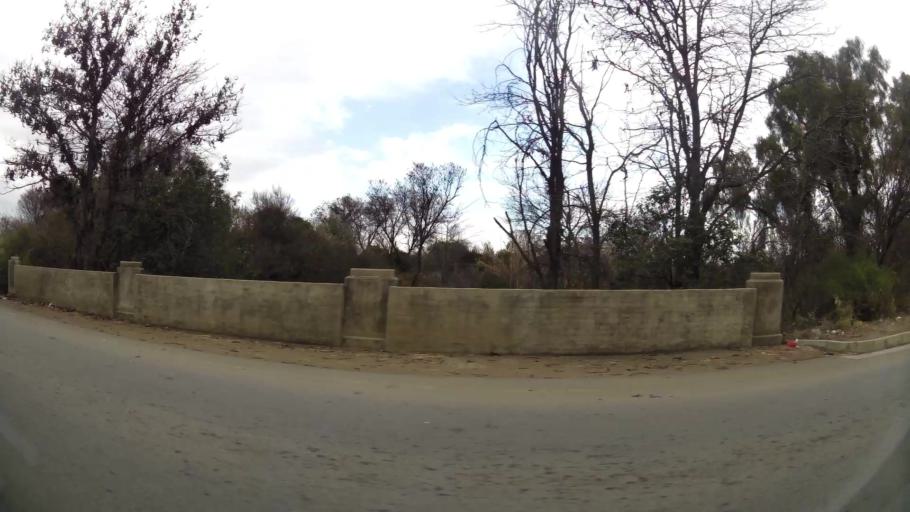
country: ZA
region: Orange Free State
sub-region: Fezile Dabi District Municipality
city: Kroonstad
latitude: -27.6574
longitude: 27.2486
